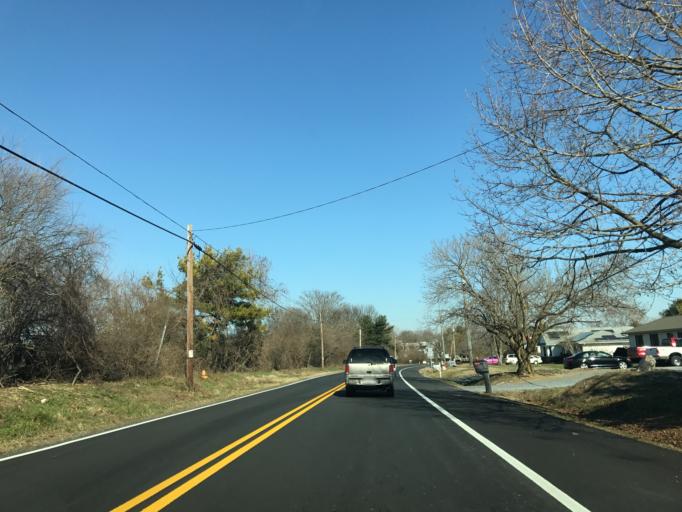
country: US
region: Maryland
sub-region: Queen Anne's County
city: Centreville
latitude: 39.0348
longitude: -76.0782
